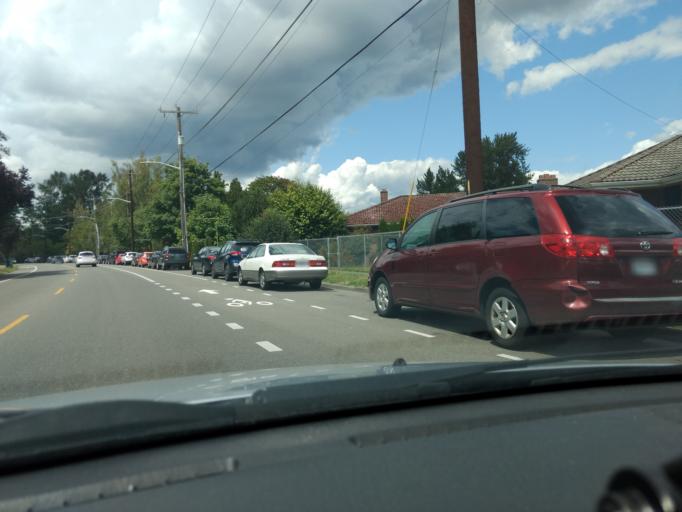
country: US
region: Washington
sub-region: King County
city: Bryn Mawr-Skyway
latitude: 47.5192
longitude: -122.2716
